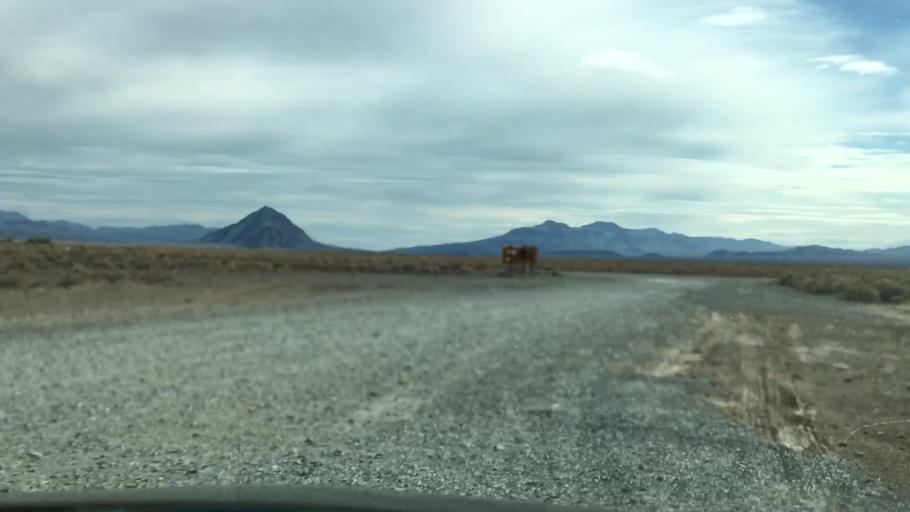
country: US
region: Nevada
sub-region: Nye County
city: Pahrump
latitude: 36.3052
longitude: -116.4218
